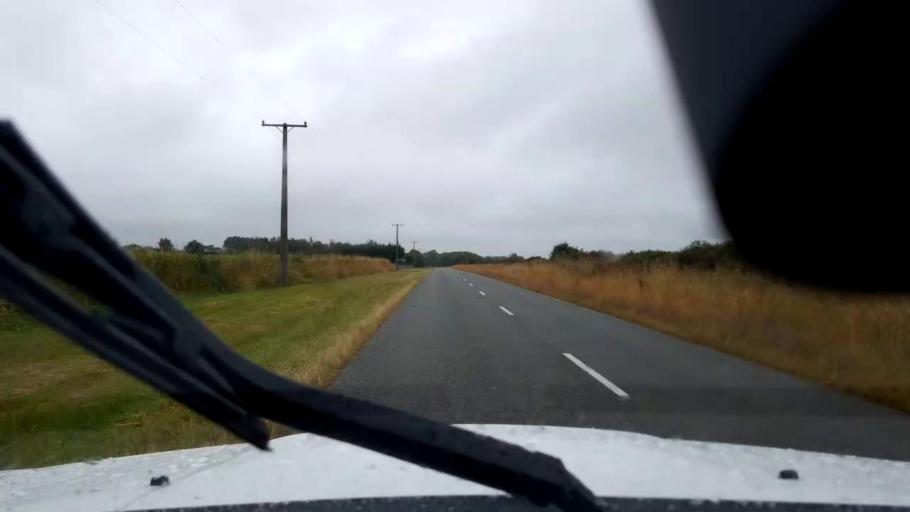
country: NZ
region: Canterbury
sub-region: Timaru District
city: Pleasant Point
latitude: -44.2535
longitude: 171.2482
